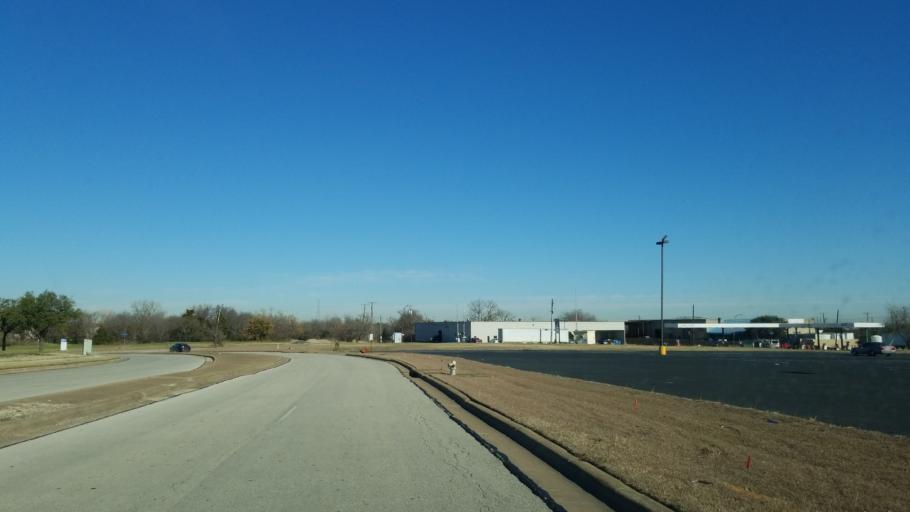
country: US
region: Texas
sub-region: Dallas County
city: Grand Prairie
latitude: 32.7434
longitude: -97.0531
